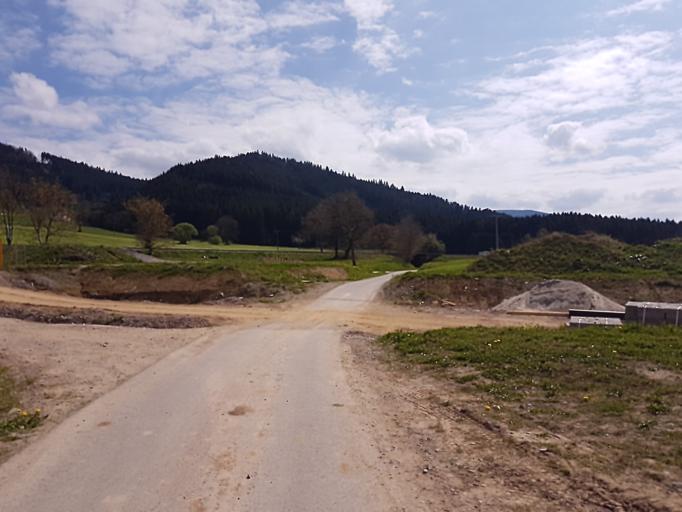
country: DE
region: Baden-Wuerttemberg
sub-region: Freiburg Region
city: Gutach im Breisgau
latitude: 48.1374
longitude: 8.0172
